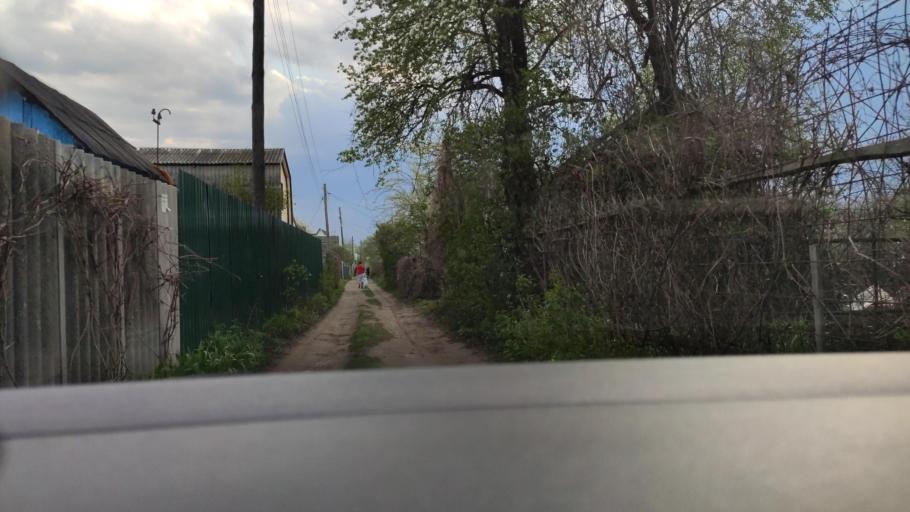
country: RU
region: Voronezj
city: Voronezh
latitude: 51.6006
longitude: 39.1636
